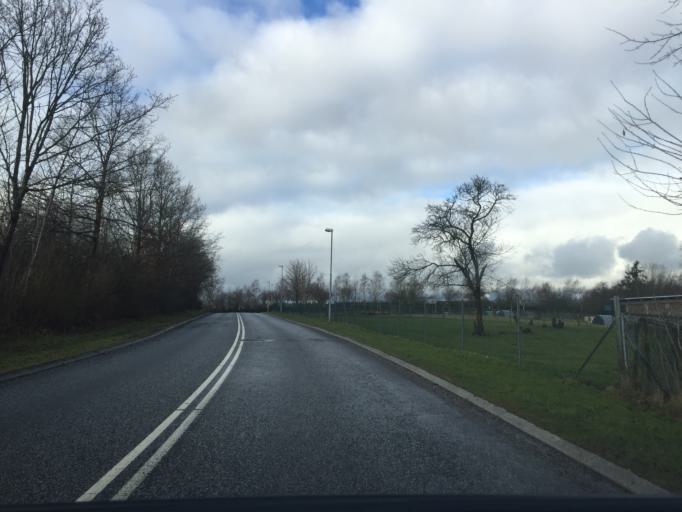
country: DK
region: Capital Region
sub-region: Fureso Kommune
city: Stavnsholt
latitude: 55.8161
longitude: 12.4011
